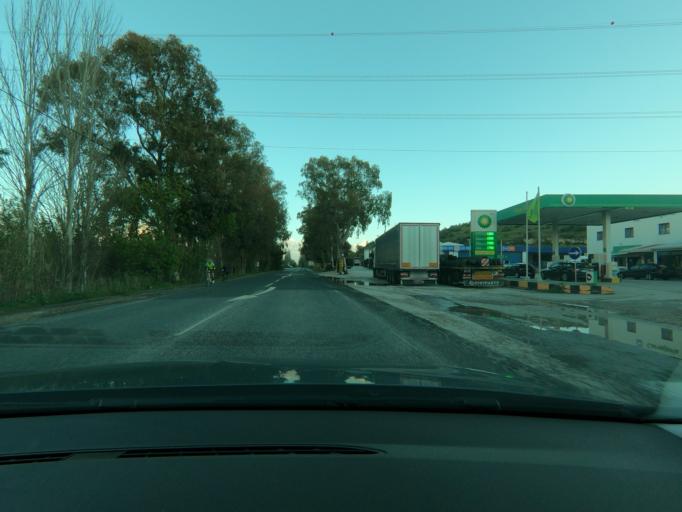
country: PT
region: Lisbon
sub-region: Alenquer
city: Carregado
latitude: 39.0169
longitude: -8.9729
